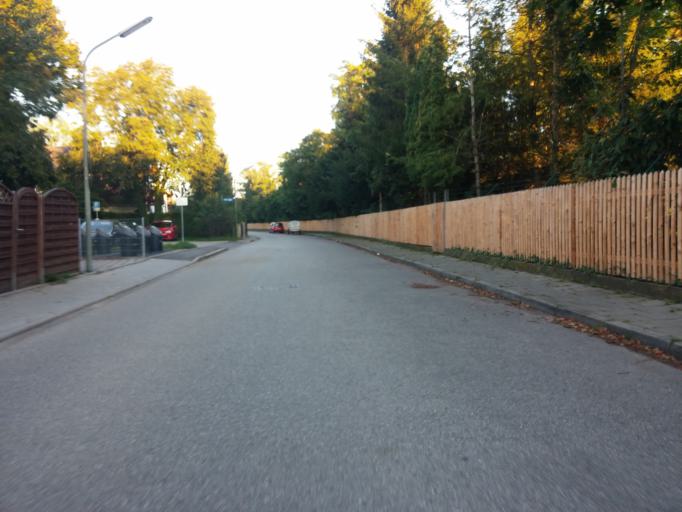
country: DE
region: Bavaria
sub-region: Upper Bavaria
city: Haar
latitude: 48.1064
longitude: 11.7403
